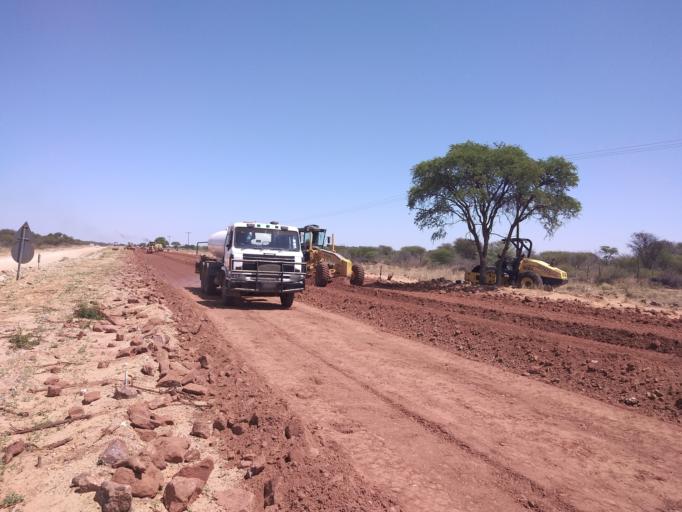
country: BW
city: Mabuli
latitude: -25.7927
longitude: 24.6615
